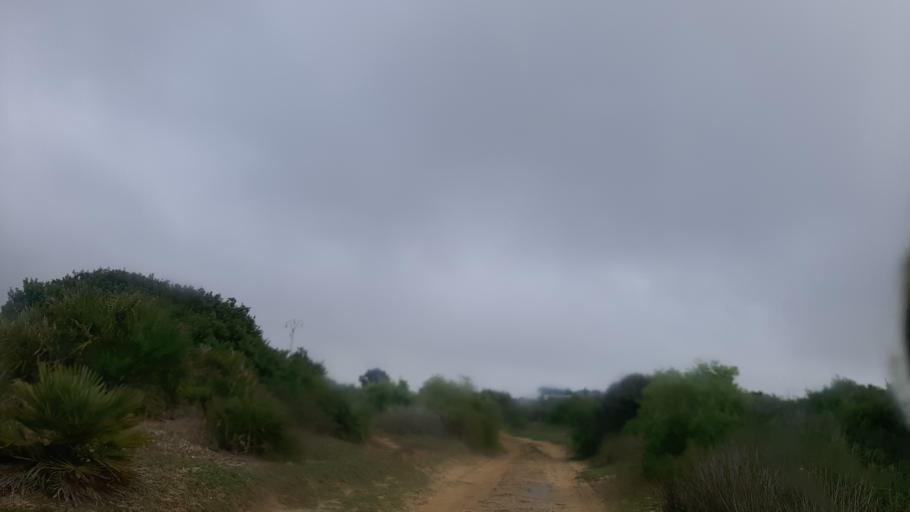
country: TN
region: Nabul
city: Qulaybiyah
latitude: 36.8250
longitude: 11.0381
